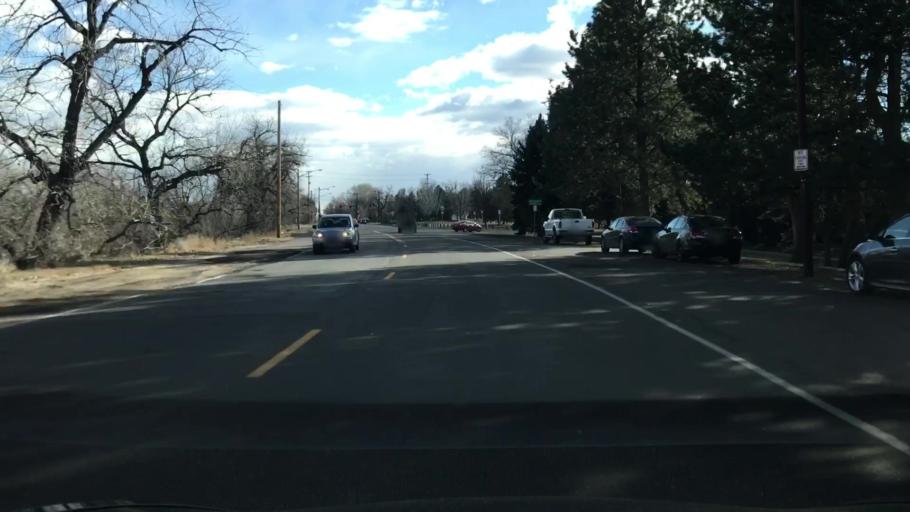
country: US
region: Colorado
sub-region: Arapahoe County
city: Glendale
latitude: 39.6975
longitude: -104.9250
